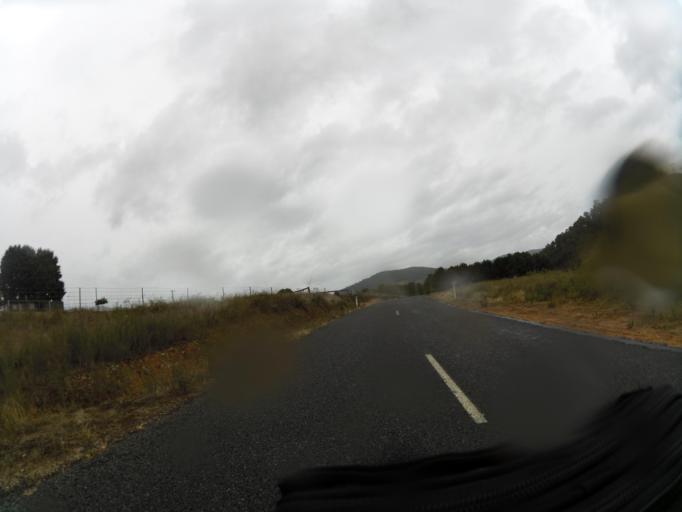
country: AU
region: New South Wales
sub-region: Greater Hume Shire
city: Holbrook
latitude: -36.2306
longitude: 147.6554
